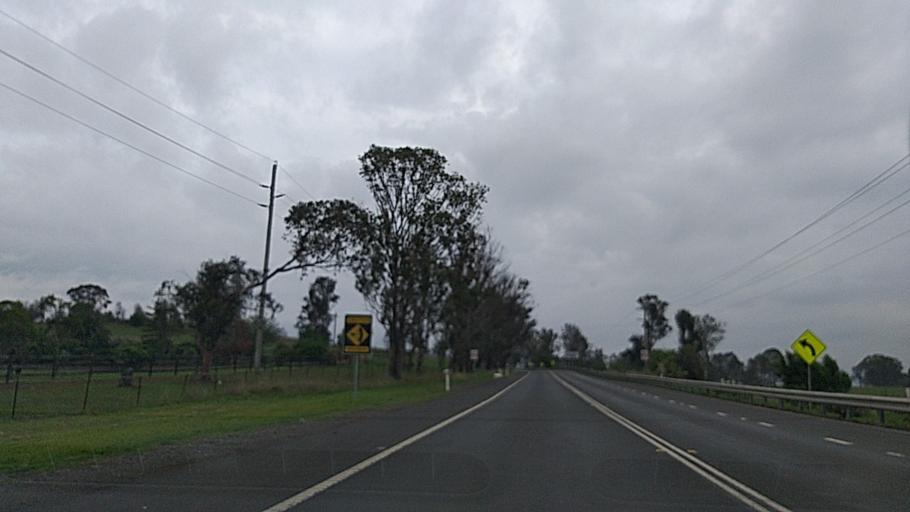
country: AU
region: New South Wales
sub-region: Liverpool
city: Luddenham
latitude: -33.8454
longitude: 150.6877
